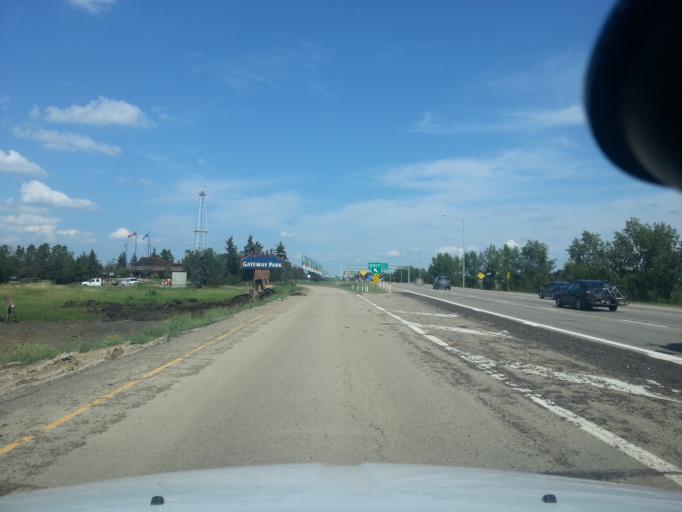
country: CA
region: Alberta
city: Beaumont
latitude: 53.4095
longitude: -113.4982
